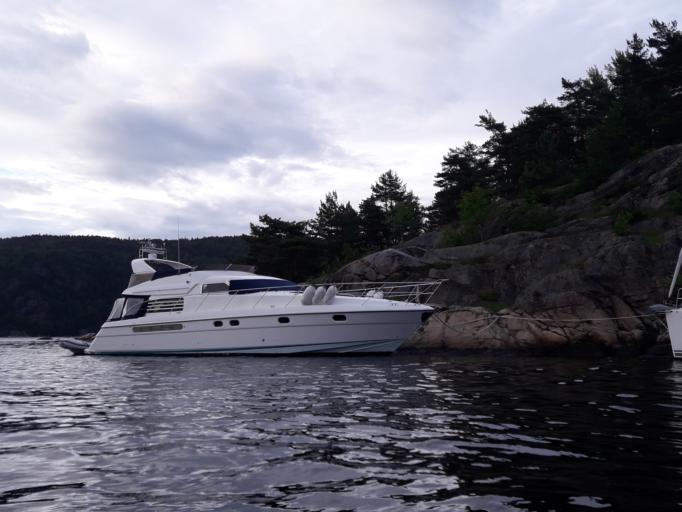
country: NO
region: Akershus
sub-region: Frogn
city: Drobak
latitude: 59.6688
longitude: 10.5782
